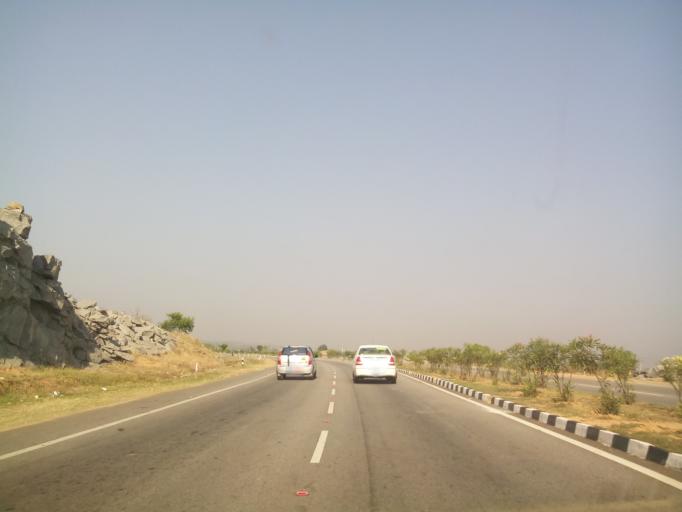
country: IN
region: Karnataka
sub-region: Bangalore Rural
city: Nelamangala
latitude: 13.0659
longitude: 77.2870
